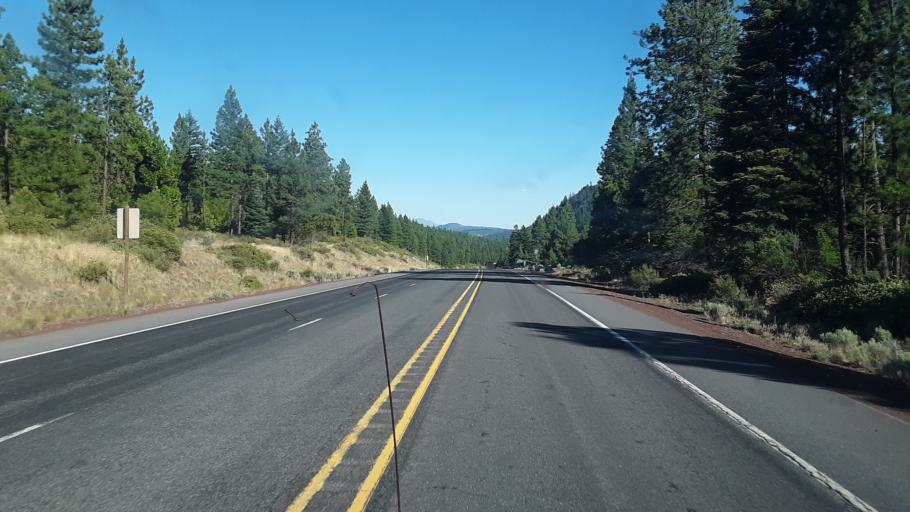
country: US
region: Oregon
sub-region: Klamath County
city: Klamath Falls
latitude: 42.3395
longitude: -121.9659
